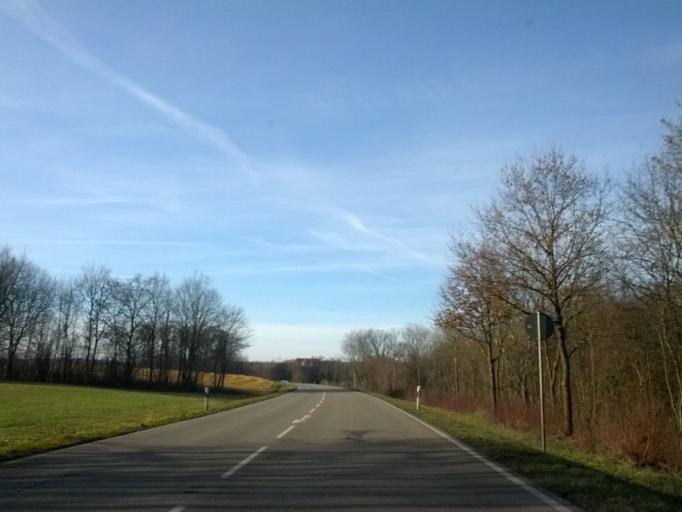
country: DE
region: Baden-Wuerttemberg
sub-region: Regierungsbezirk Stuttgart
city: Ellwangen
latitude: 48.9630
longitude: 10.1609
